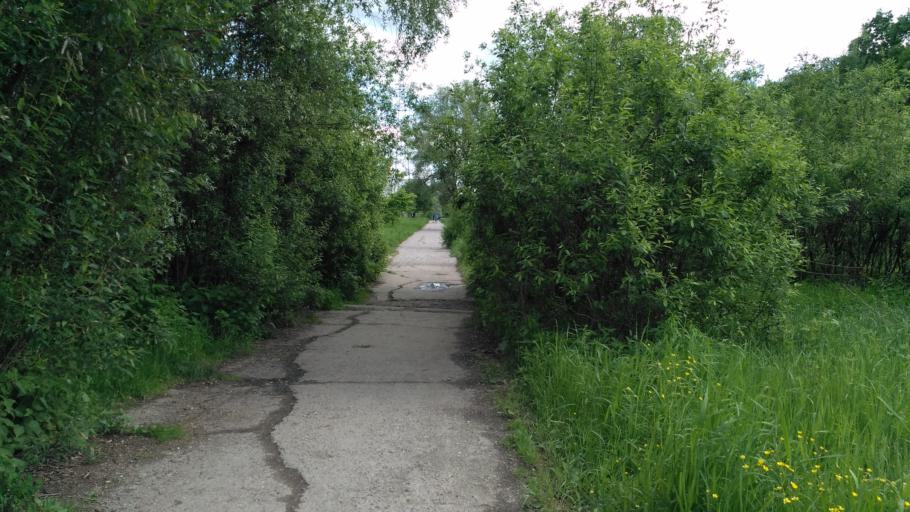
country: RU
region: Moscow
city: Metrogorodok
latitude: 55.8335
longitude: 37.7642
